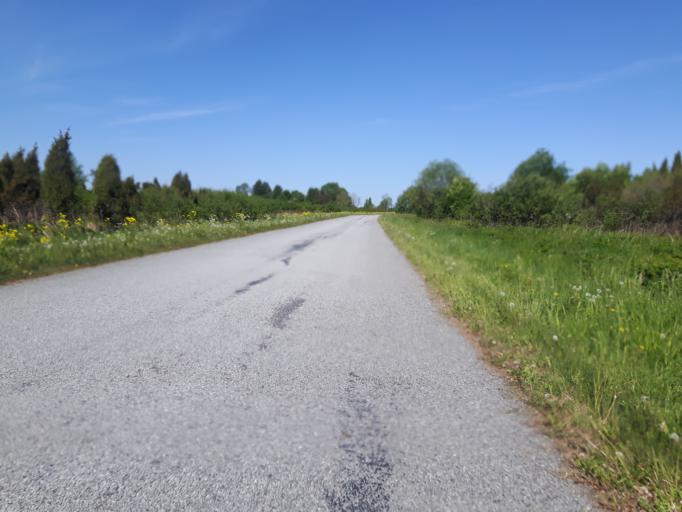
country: EE
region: Ida-Virumaa
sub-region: Aseri vald
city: Aseri
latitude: 59.4632
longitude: 26.8269
